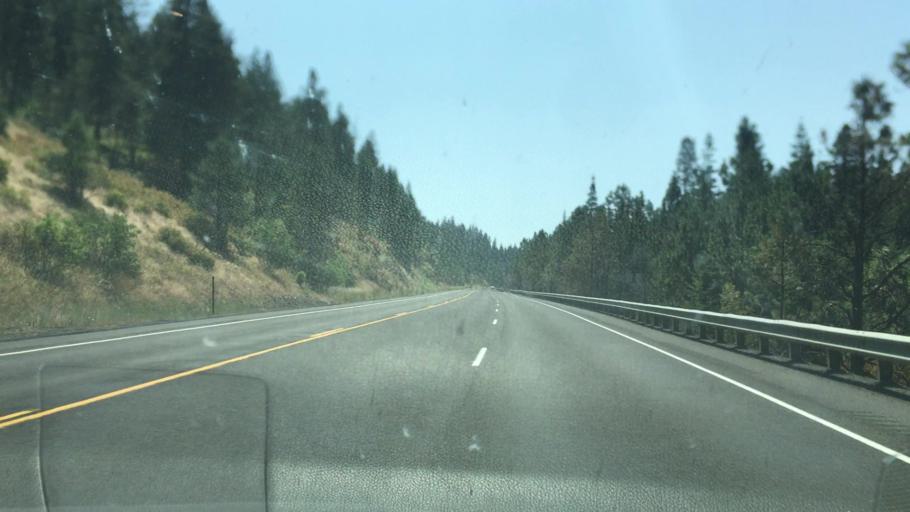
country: US
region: Idaho
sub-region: Idaho County
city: Grangeville
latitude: 45.8621
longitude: -116.2371
